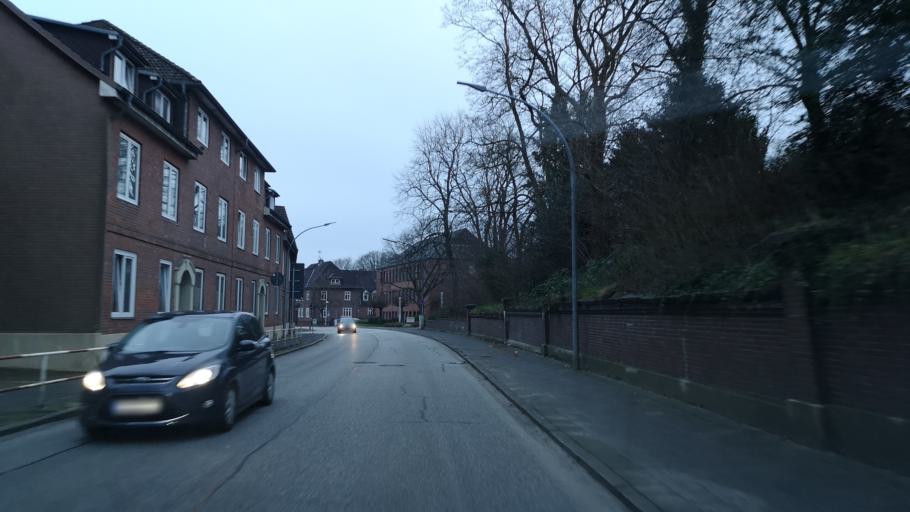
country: DE
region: Schleswig-Holstein
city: Itzehoe
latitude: 53.9252
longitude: 9.5279
